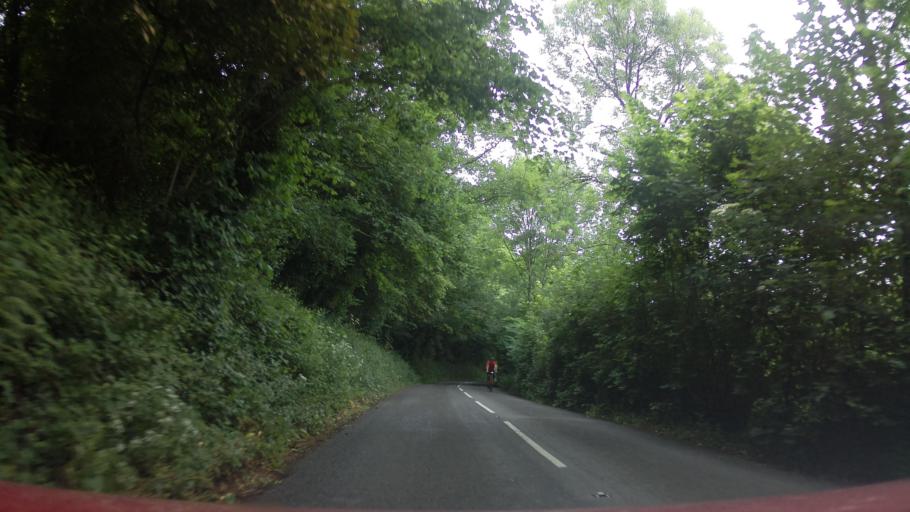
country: GB
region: England
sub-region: Devon
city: Chudleigh
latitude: 50.6429
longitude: -3.6372
